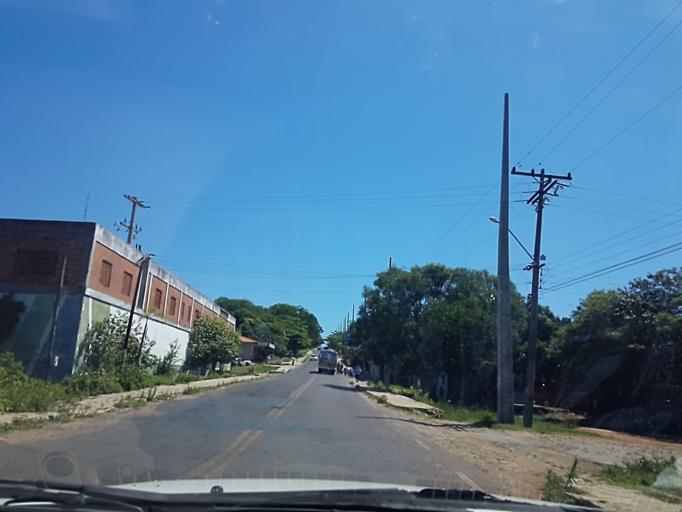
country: PY
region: Cordillera
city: Altos
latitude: -25.2578
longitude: -57.2461
